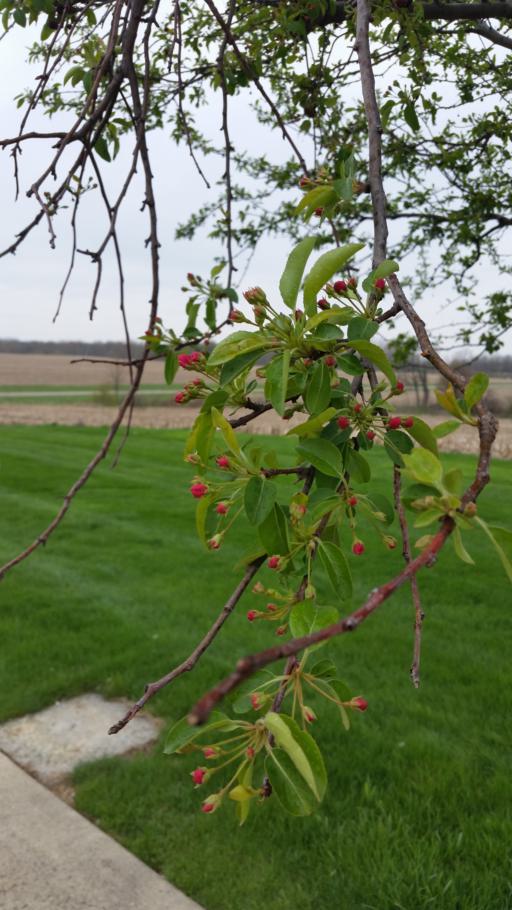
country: US
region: Ohio
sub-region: Morrow County
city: Mount Gilead
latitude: 40.4930
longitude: -82.7122
